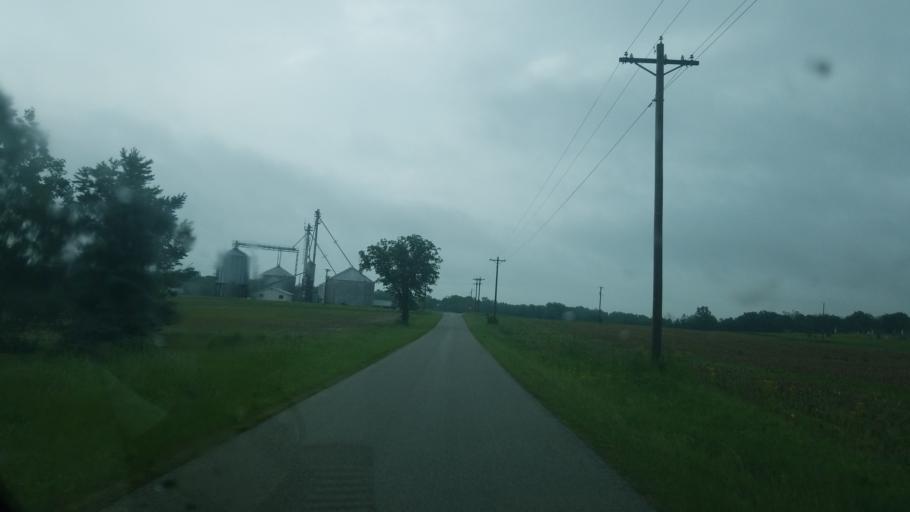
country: US
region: Ohio
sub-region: Huron County
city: Willard
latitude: 40.9459
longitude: -82.7935
